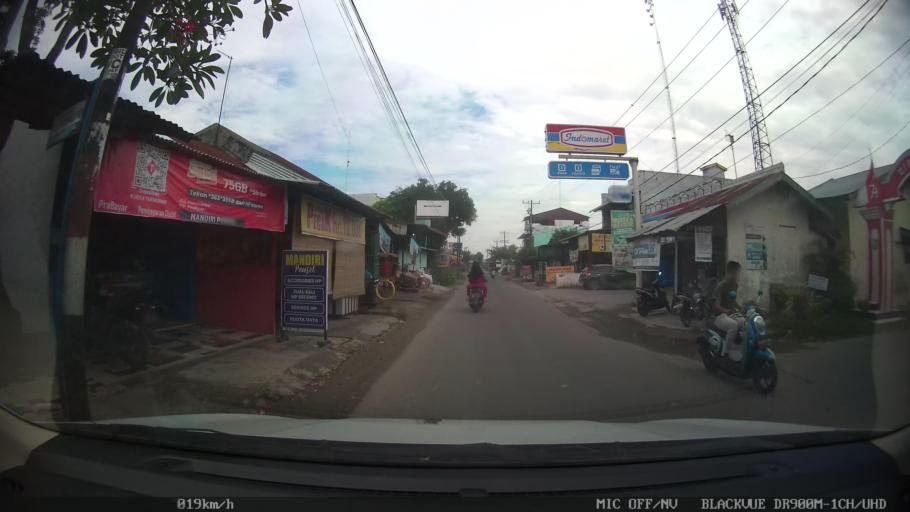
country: ID
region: North Sumatra
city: Sunggal
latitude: 3.6436
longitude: 98.5940
